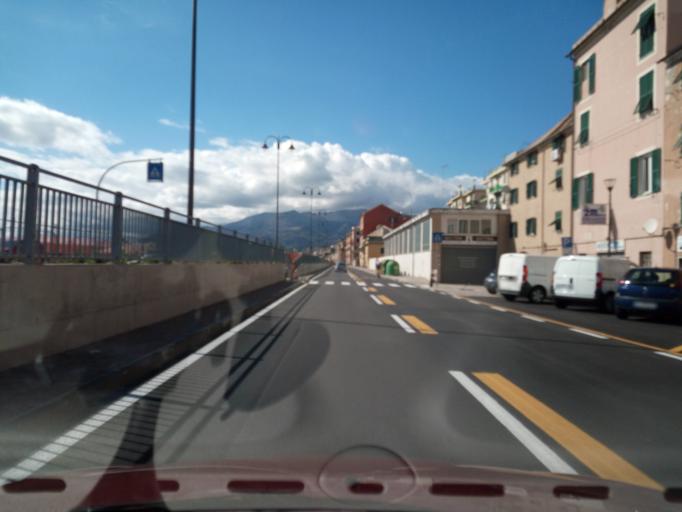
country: IT
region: Liguria
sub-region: Provincia di Genova
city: Mele
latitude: 44.4259
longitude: 8.7932
